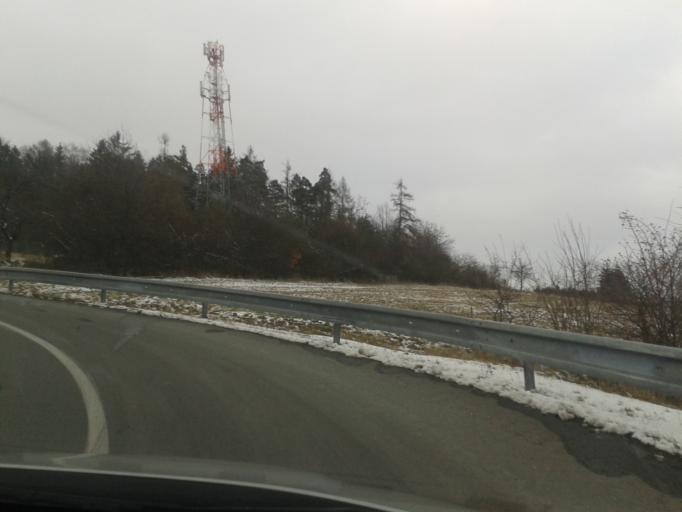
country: CZ
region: Olomoucky
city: Konice
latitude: 49.5958
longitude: 16.8900
